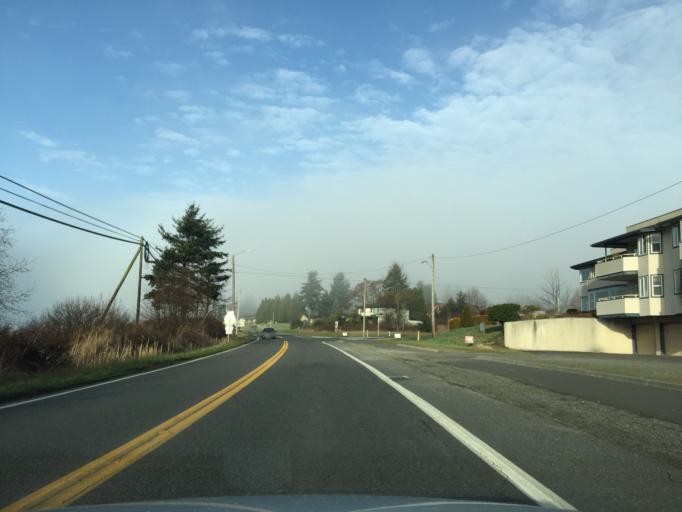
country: US
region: Washington
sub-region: Whatcom County
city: Blaine
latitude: 48.9841
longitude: -122.7409
